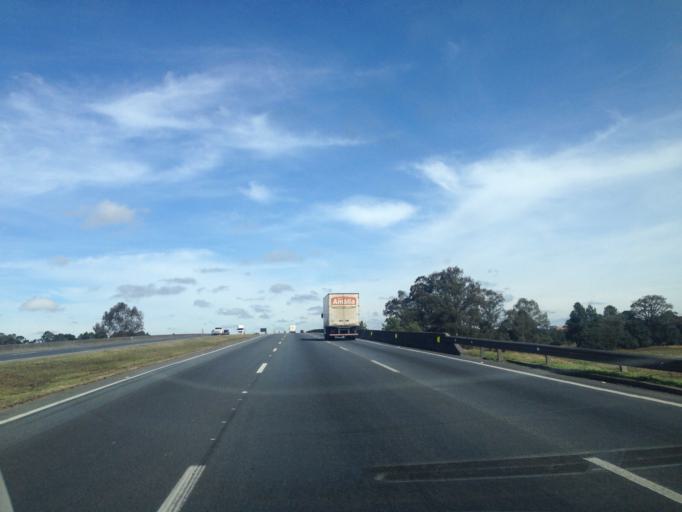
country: BR
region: Parana
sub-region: Sao Jose Dos Pinhais
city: Sao Jose dos Pinhais
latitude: -25.5321
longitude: -49.1451
